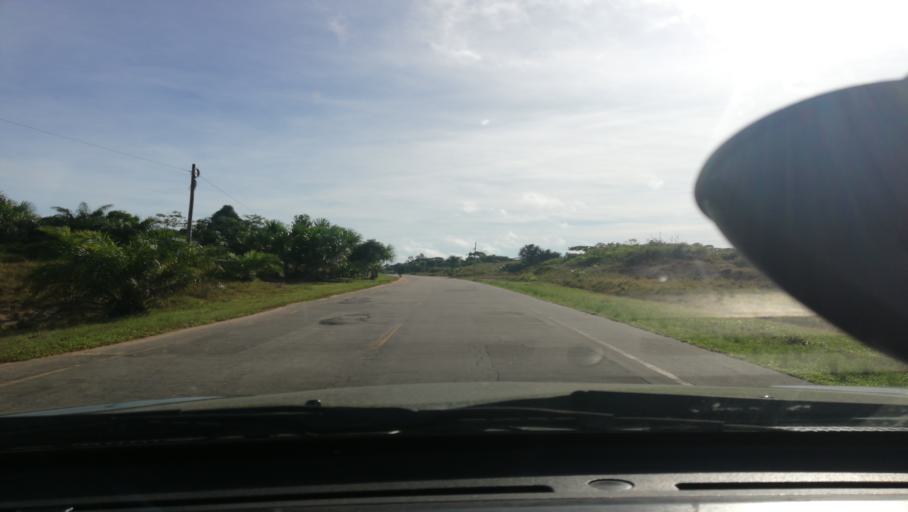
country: PE
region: Loreto
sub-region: Provincia de Loreto
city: Nauta
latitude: -4.3445
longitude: -73.5408
